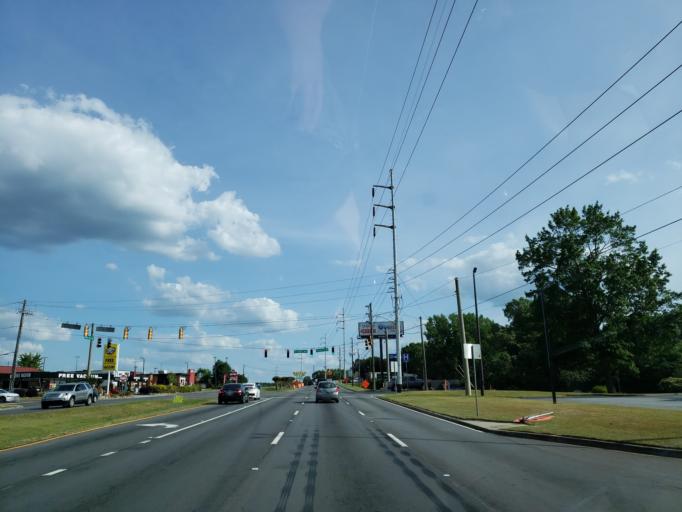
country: US
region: Georgia
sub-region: Carroll County
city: Carrollton
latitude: 33.5696
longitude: -85.0783
